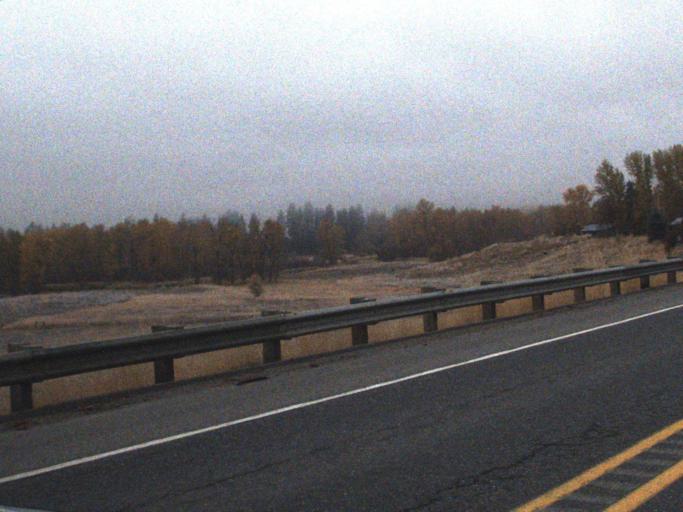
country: US
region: Washington
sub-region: Stevens County
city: Kettle Falls
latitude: 48.5972
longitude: -118.0070
